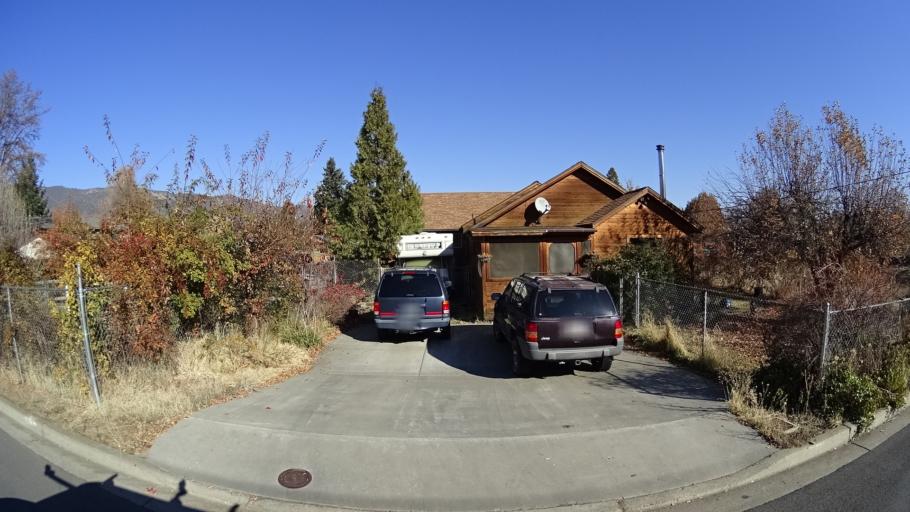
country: US
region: California
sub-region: Siskiyou County
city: Yreka
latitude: 41.7336
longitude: -122.6409
